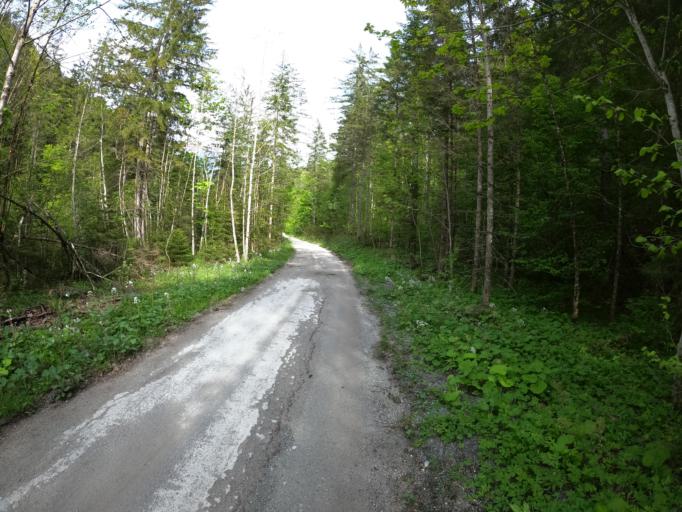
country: AT
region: Salzburg
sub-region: Politischer Bezirk Sankt Johann im Pongau
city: Werfen
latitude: 47.4775
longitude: 13.1368
